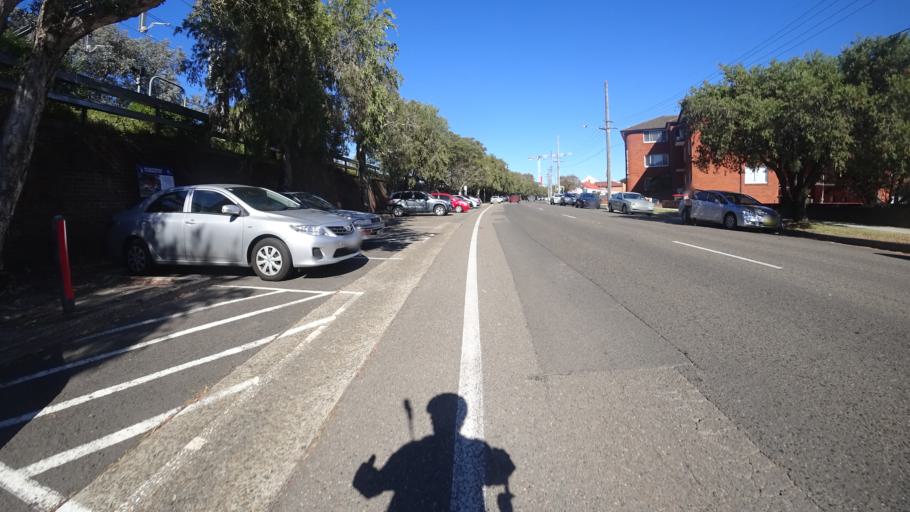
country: AU
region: New South Wales
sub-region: Kogarah
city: Beverly Park
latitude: -33.9649
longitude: 151.1314
